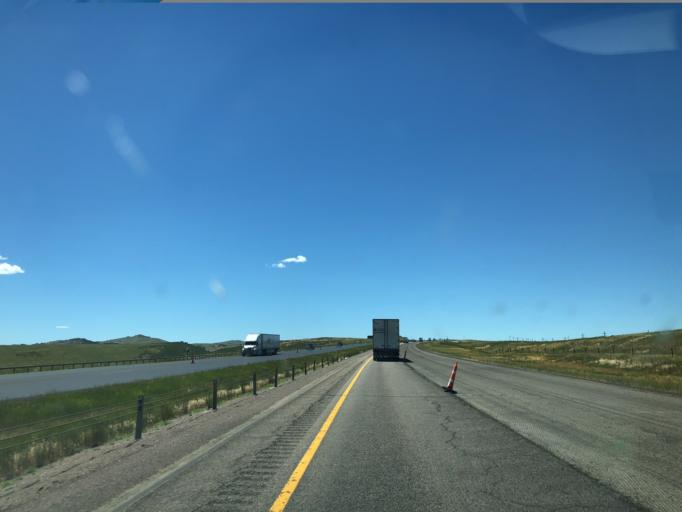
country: US
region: Wyoming
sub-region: Laramie County
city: Cheyenne
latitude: 41.0987
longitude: -105.1341
